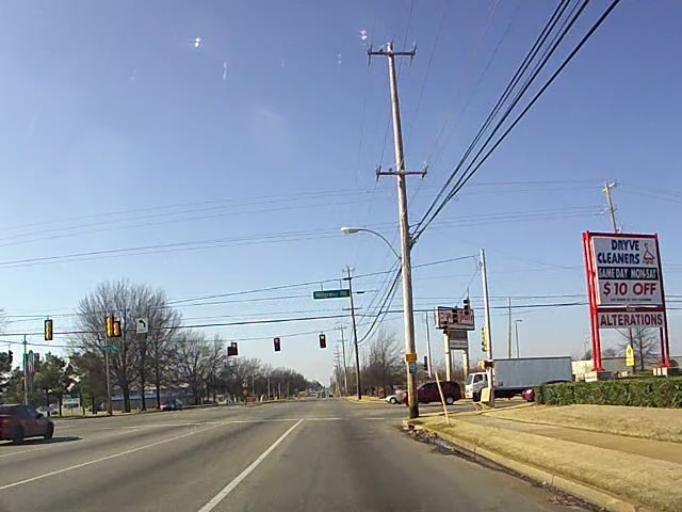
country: US
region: Tennessee
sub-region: Shelby County
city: Germantown
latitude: 35.0499
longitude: -89.8572
